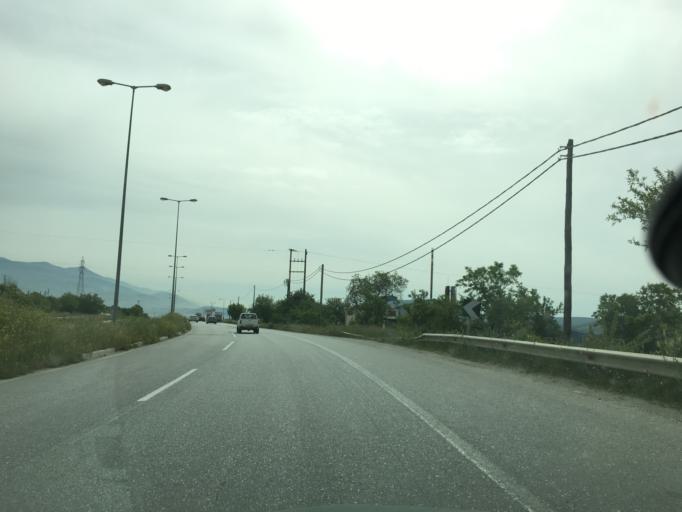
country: GR
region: Thessaly
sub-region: Nomos Magnisias
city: Nea Ionia
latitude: 39.3808
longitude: 22.8642
